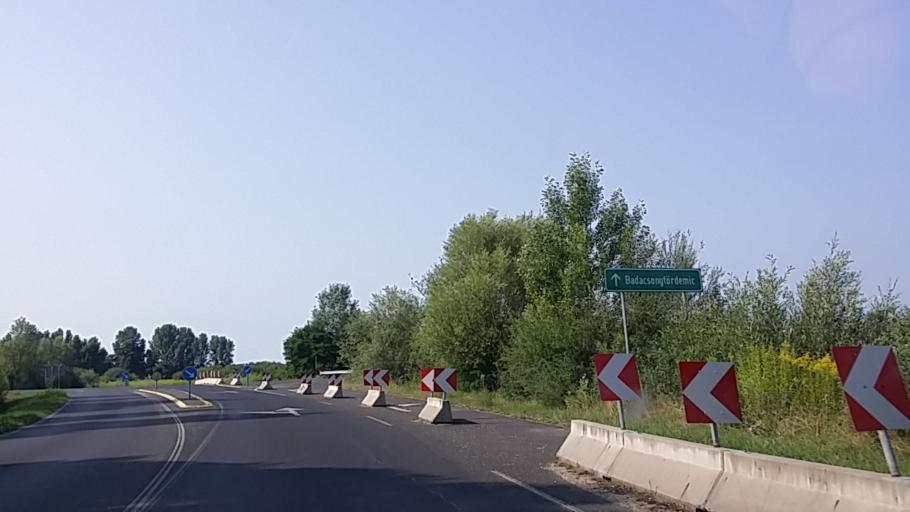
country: HU
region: Veszprem
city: Badacsonytomaj
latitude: 46.8211
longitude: 17.4783
